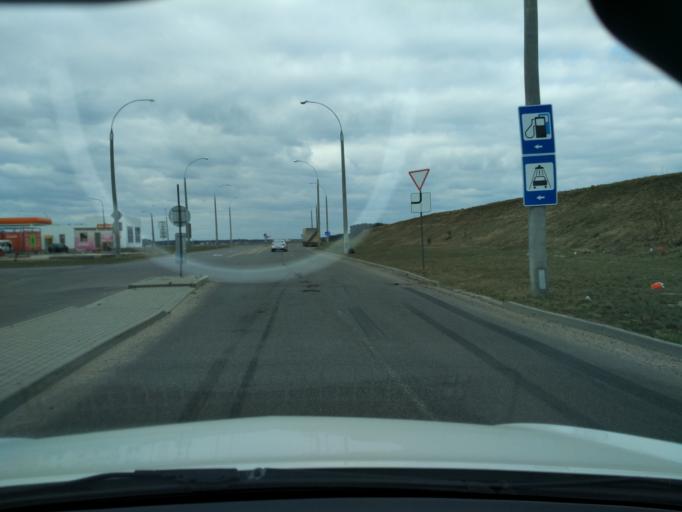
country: BY
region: Minsk
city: Bal'shavik
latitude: 53.9686
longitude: 27.5484
